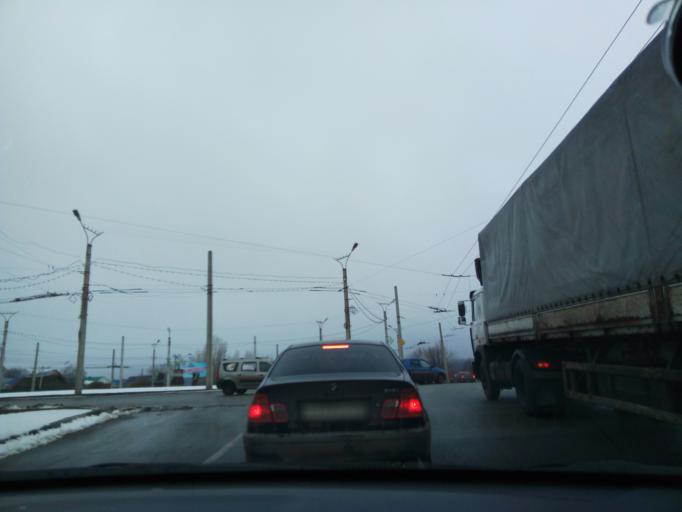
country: RU
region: Chuvashia
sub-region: Cheboksarskiy Rayon
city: Cheboksary
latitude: 56.1273
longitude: 47.2133
